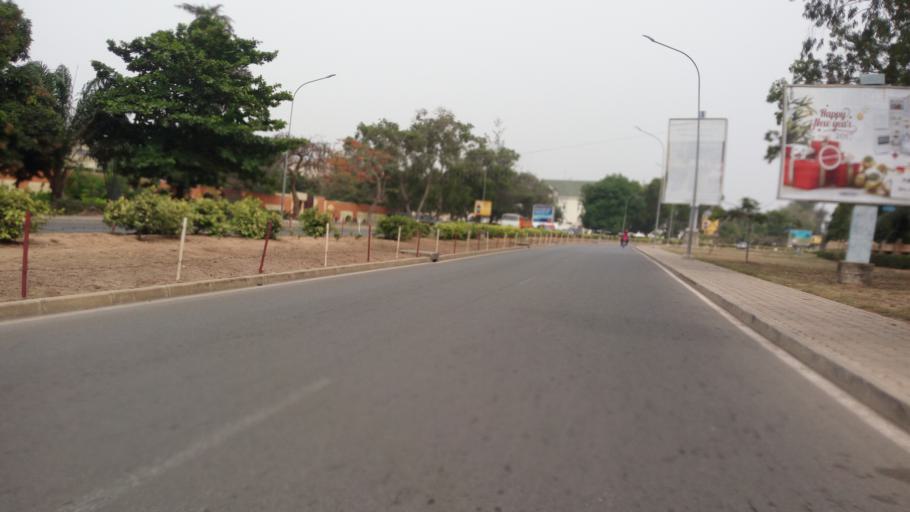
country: BJ
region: Littoral
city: Cotonou
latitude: 6.3500
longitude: 2.3930
